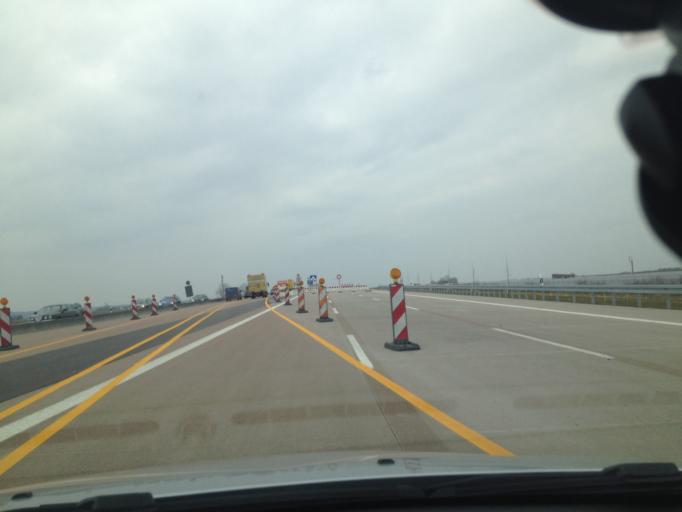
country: DE
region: Bavaria
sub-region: Swabia
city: Rosshaupten
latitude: 48.4110
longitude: 10.4861
